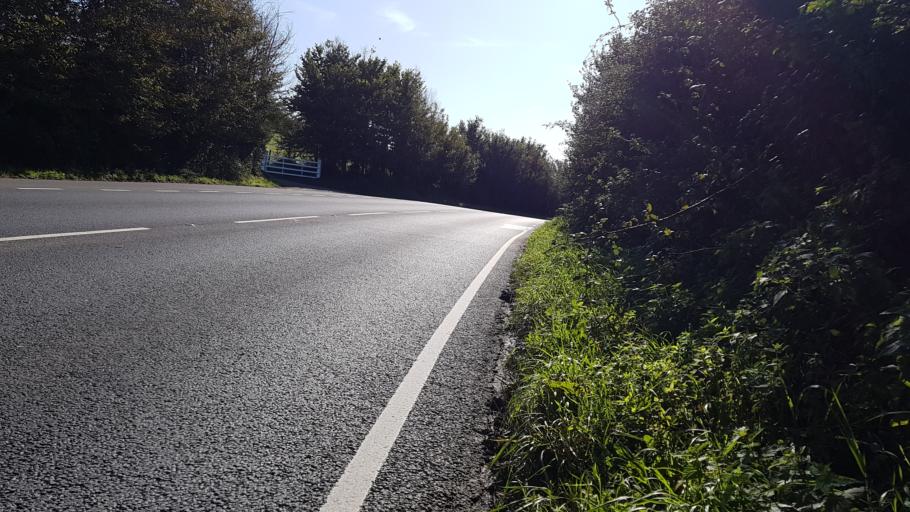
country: GB
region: England
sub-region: Isle of Wight
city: Newport
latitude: 50.6808
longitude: -1.2863
